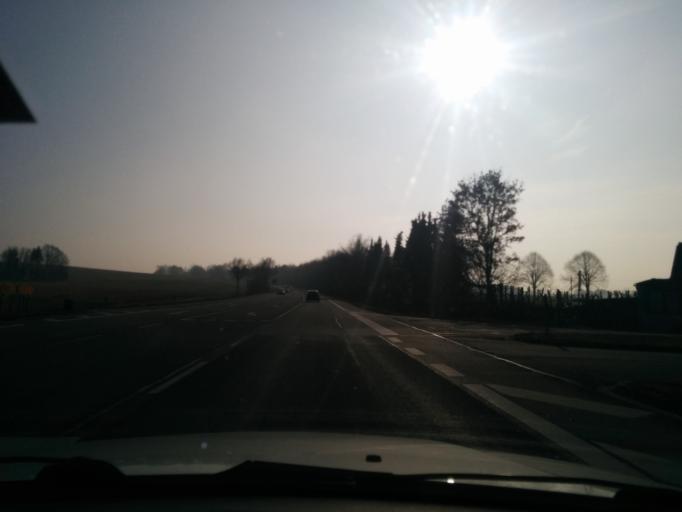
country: DE
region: North Rhine-Westphalia
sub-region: Regierungsbezirk Detmold
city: Blomberg
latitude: 51.9183
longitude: 9.0843
